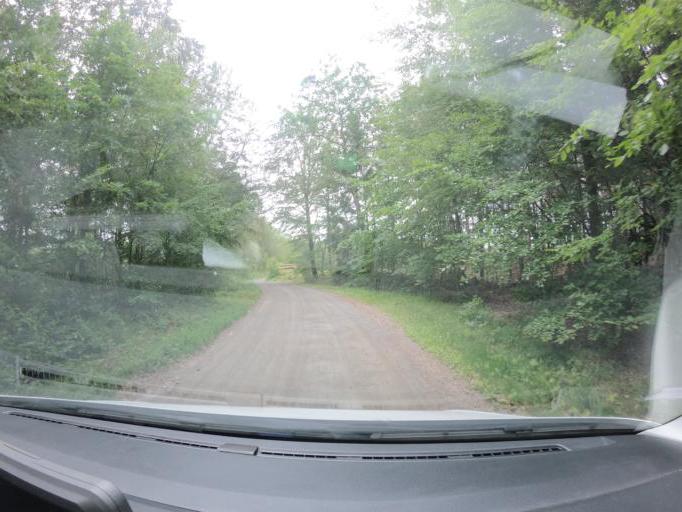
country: SE
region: Skane
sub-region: Hassleholms Kommun
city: Sosdala
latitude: 56.0285
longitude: 13.6207
